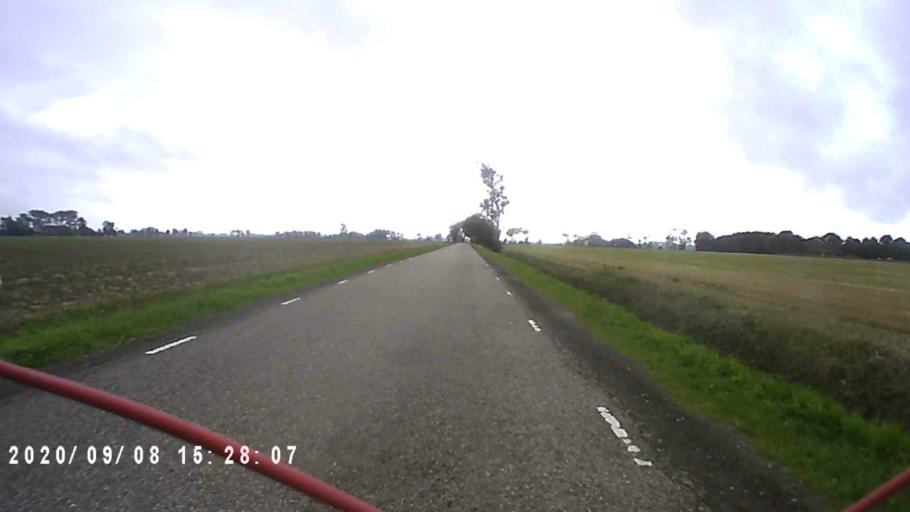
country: NL
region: Groningen
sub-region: Gemeente Bedum
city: Bedum
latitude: 53.2948
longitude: 6.6572
